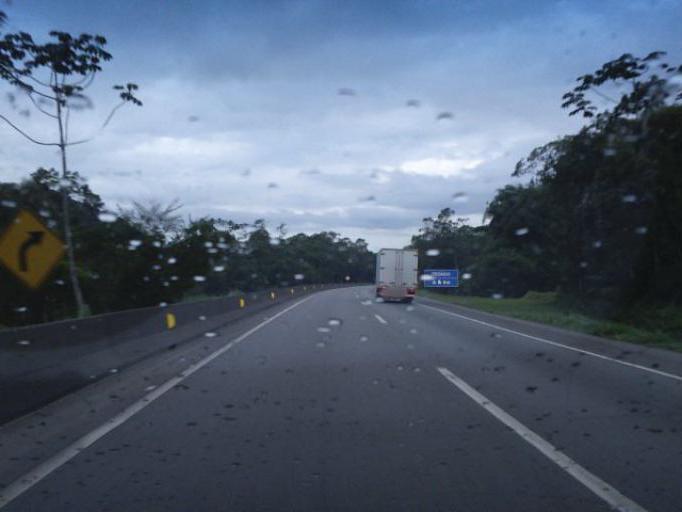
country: BR
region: Parana
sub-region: Guaratuba
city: Guaratuba
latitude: -25.9435
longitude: -48.9083
